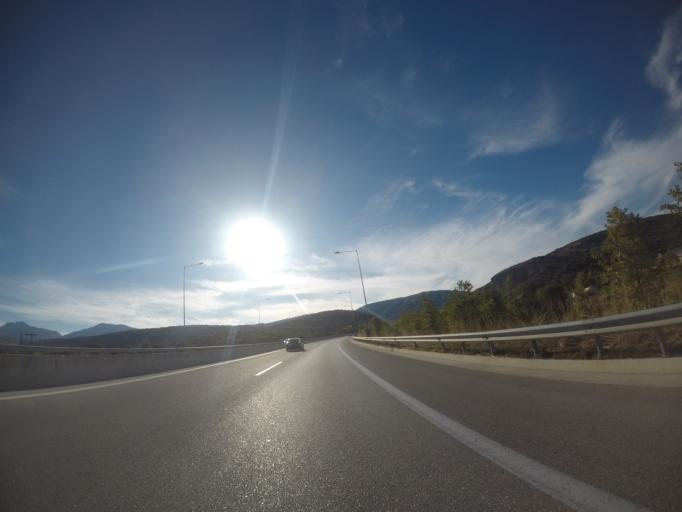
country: GR
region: Epirus
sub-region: Nomos Ioanninon
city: Pedini
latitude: 39.5925
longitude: 20.8400
